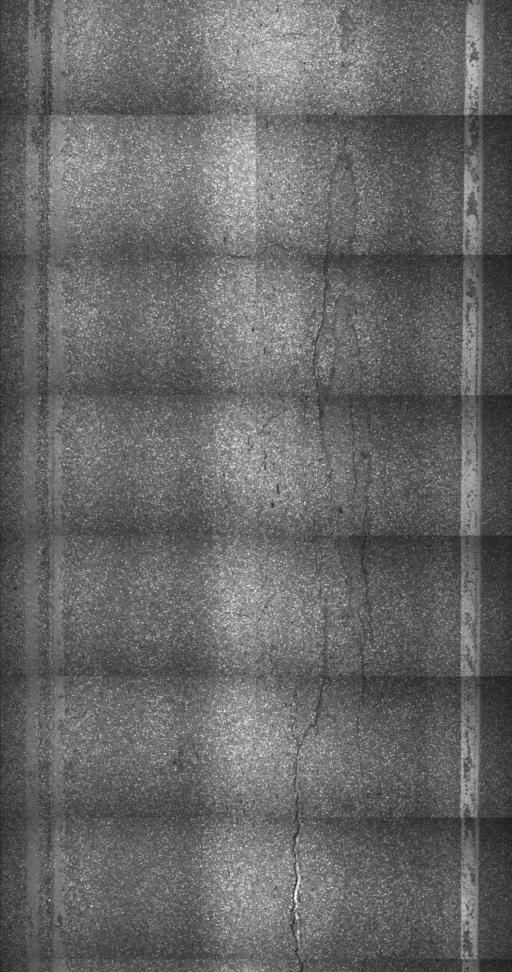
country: US
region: Vermont
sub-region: Franklin County
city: Saint Albans
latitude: 44.8308
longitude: -73.0521
